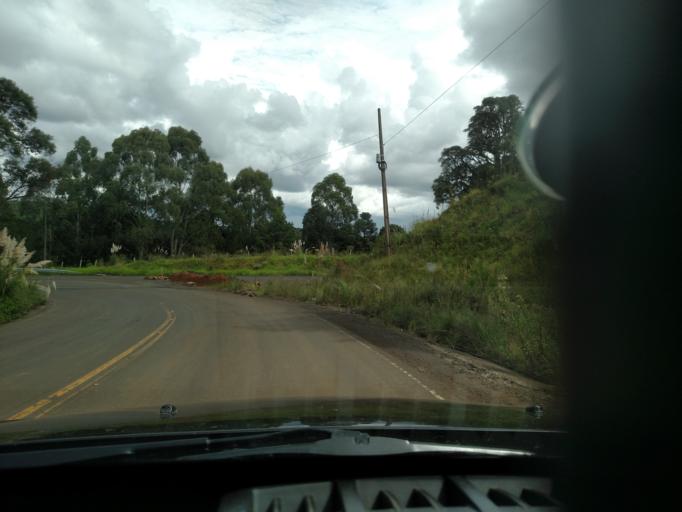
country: BR
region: Santa Catarina
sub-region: Lages
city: Lages
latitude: -27.9566
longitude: -50.4898
